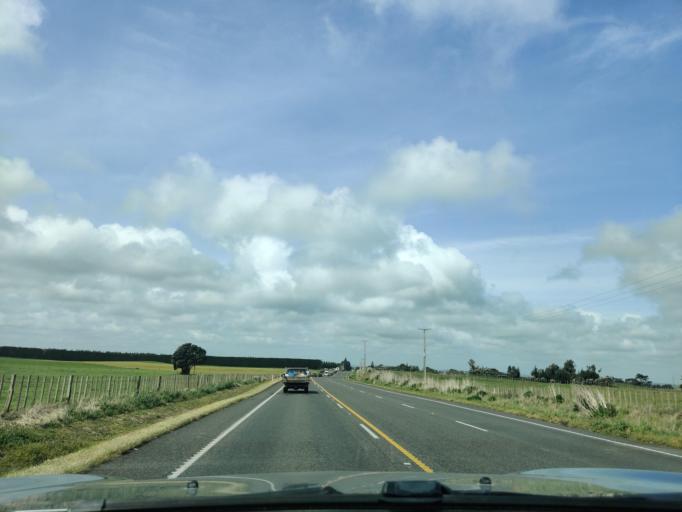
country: NZ
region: Taranaki
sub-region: South Taranaki District
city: Patea
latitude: -39.7660
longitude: 174.6131
